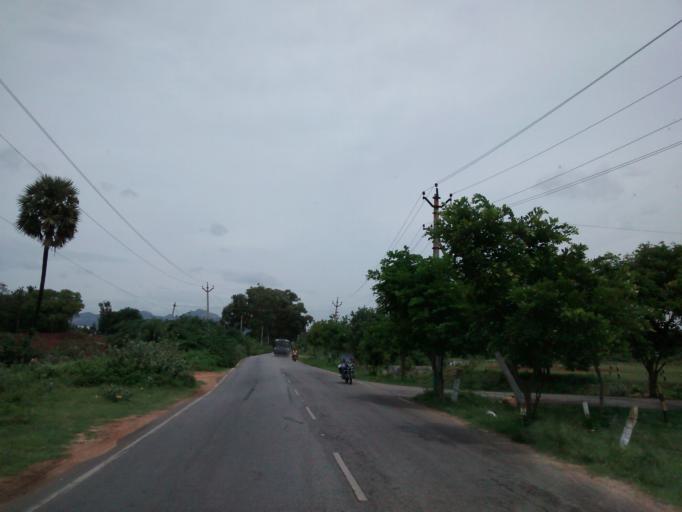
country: IN
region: Andhra Pradesh
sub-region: Chittoor
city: Narasingapuram
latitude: 13.6104
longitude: 79.3428
